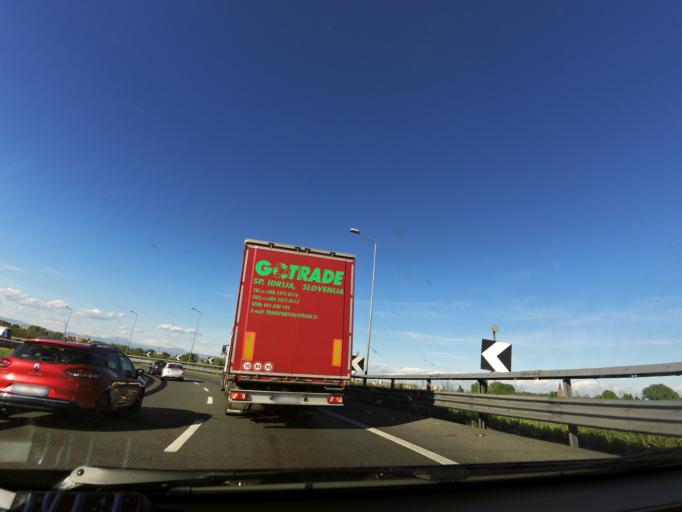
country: IT
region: Lombardy
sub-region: Citta metropolitana di Milano
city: Civesio
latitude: 45.3846
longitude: 9.2693
